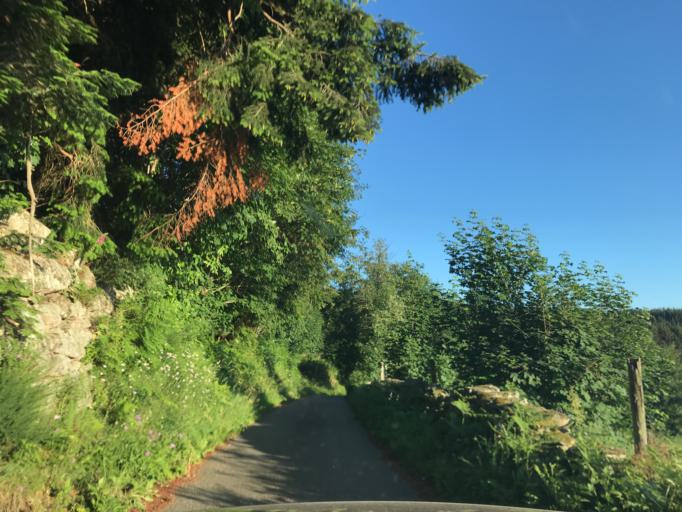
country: FR
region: Rhone-Alpes
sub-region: Departement de la Loire
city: Noiretable
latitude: 45.7837
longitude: 3.6916
